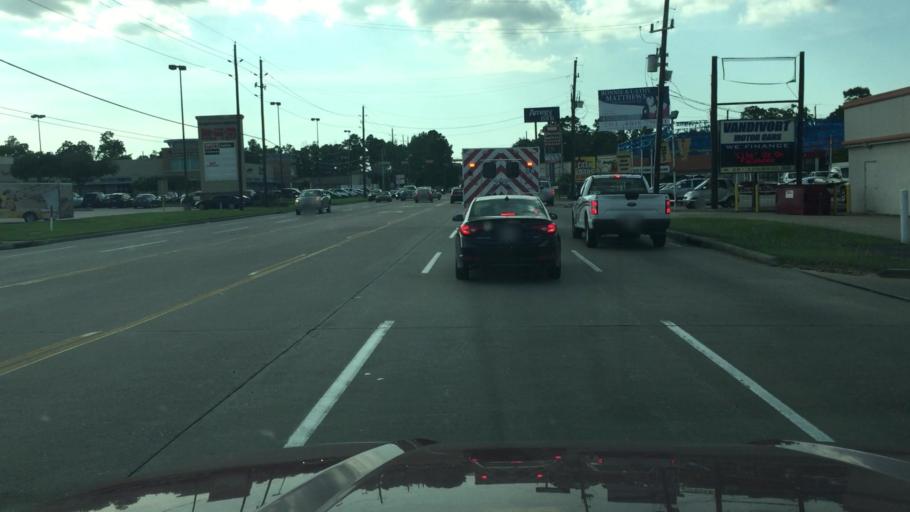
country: US
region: Texas
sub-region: Harris County
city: Tomball
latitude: 30.0221
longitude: -95.5251
